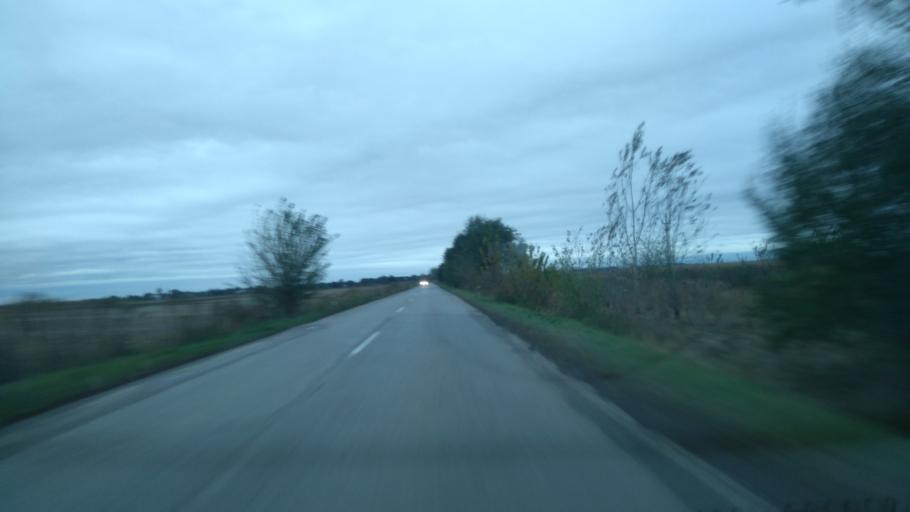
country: RS
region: Autonomna Pokrajina Vojvodina
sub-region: Juznobacki Okrug
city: Durdevo
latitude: 45.3442
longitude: 20.0615
